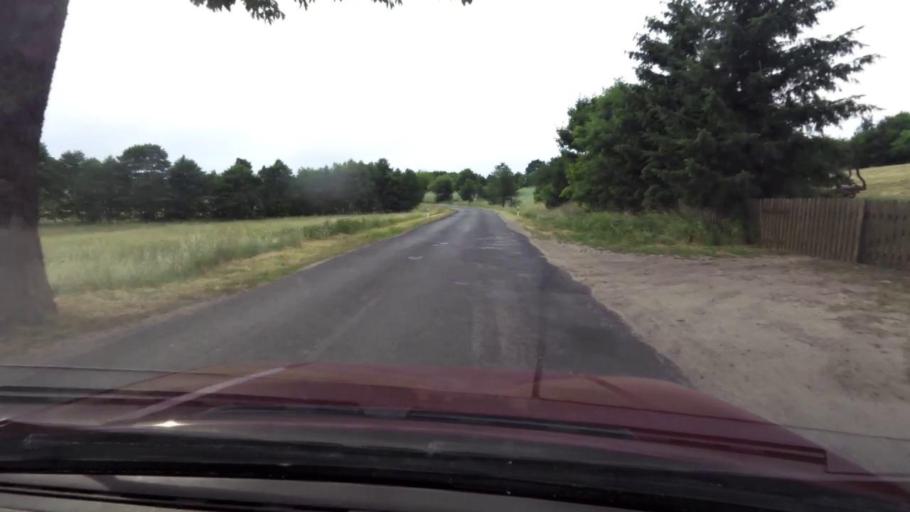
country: PL
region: Pomeranian Voivodeship
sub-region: Powiat bytowski
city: Trzebielino
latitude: 54.2639
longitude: 17.0439
